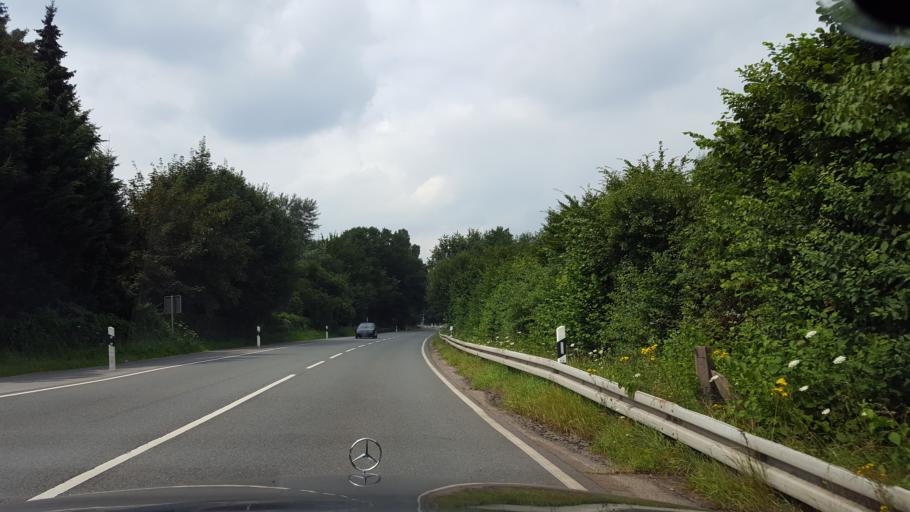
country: DE
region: North Rhine-Westphalia
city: Marl
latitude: 51.6922
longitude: 7.1185
